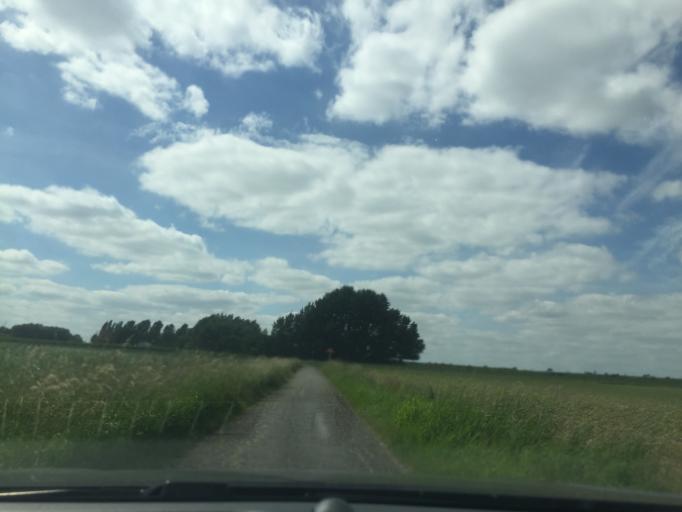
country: BE
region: Flanders
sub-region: Provincie West-Vlaanderen
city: Lendelede
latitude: 50.8702
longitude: 3.2120
